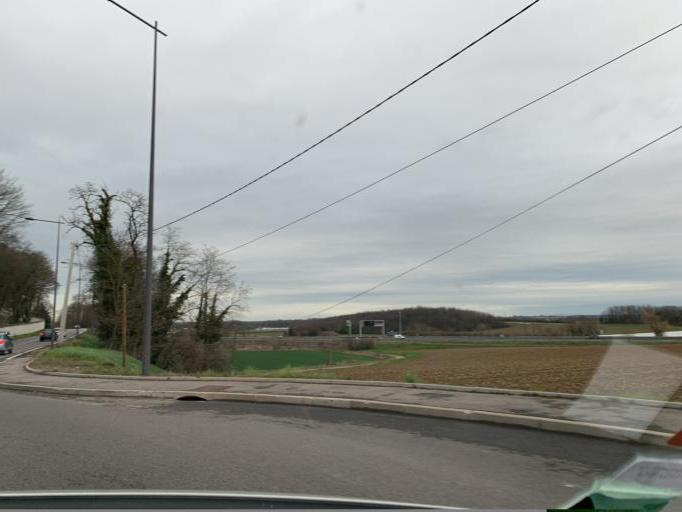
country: FR
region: Rhone-Alpes
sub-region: Departement du Rhone
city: Rillieux-la-Pape
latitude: 45.8378
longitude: 4.9148
